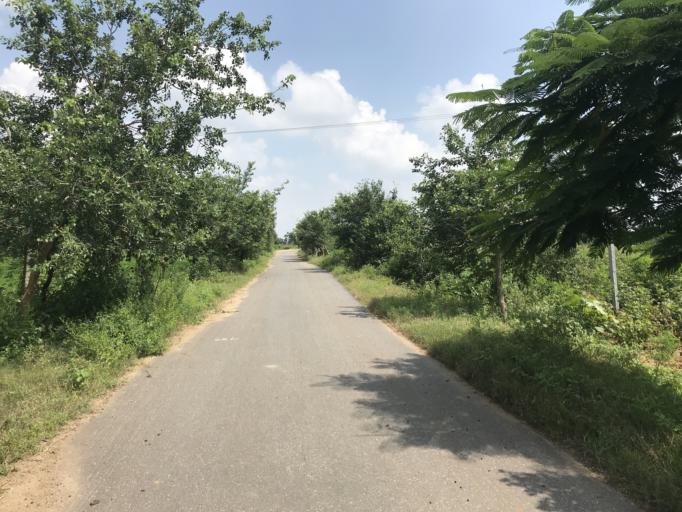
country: IN
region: Telangana
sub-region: Warangal
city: Mahbubabad
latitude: 17.6857
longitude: 79.7165
